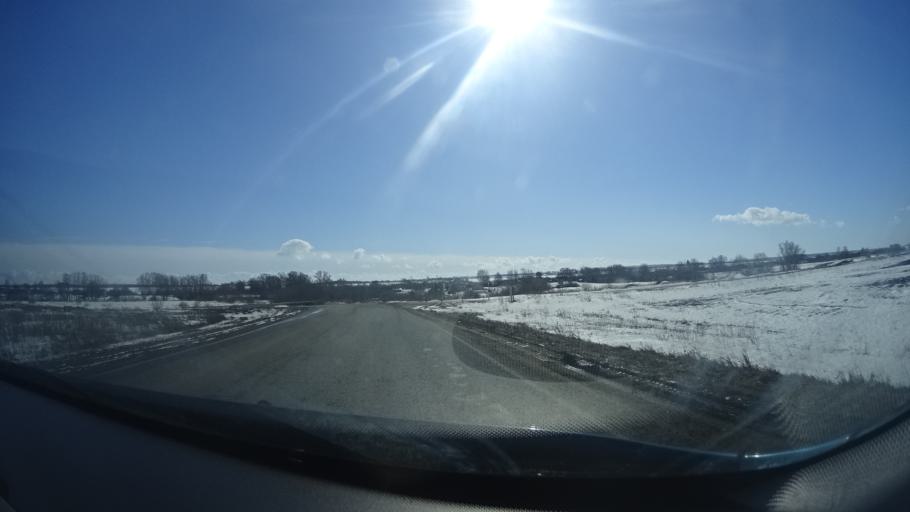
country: RU
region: Bashkortostan
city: Avdon
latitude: 54.5863
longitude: 55.8572
